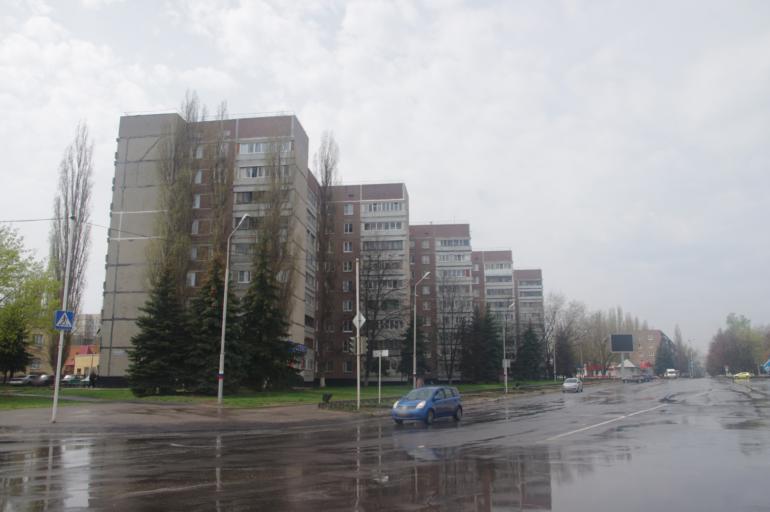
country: RU
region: Kursk
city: Kurchatov
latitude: 51.6591
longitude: 35.6587
